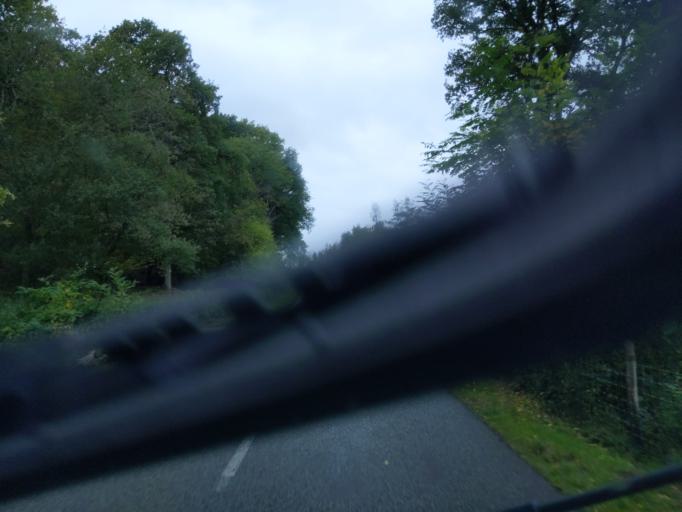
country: FR
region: Ile-de-France
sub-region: Departement des Yvelines
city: Bullion
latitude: 48.6301
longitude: 1.9644
